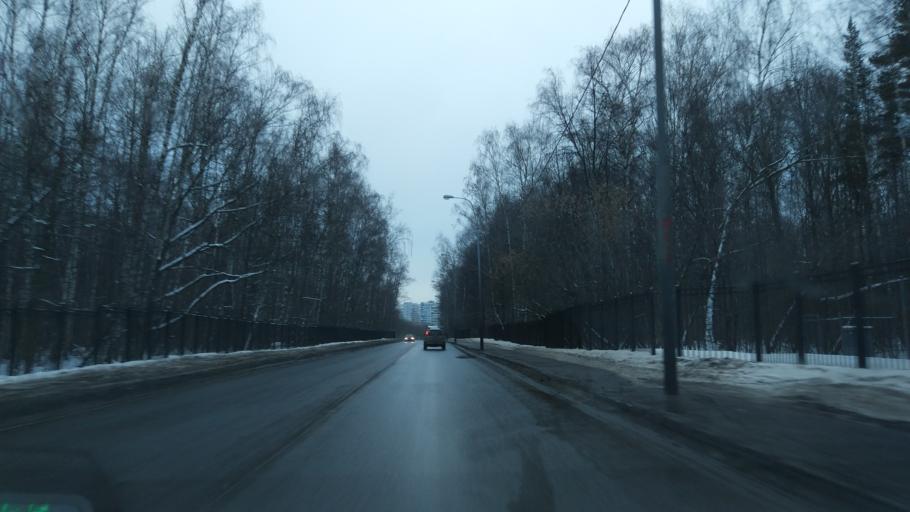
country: RU
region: Moskovskaya
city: Izmaylovo
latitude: 55.7845
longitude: 37.8203
